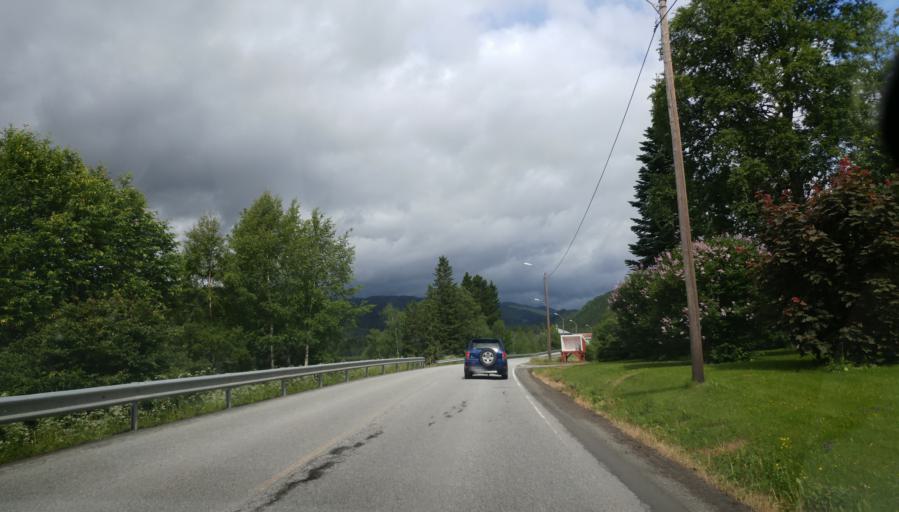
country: NO
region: Sor-Trondelag
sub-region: Selbu
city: Mebonden
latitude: 63.2734
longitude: 11.0773
